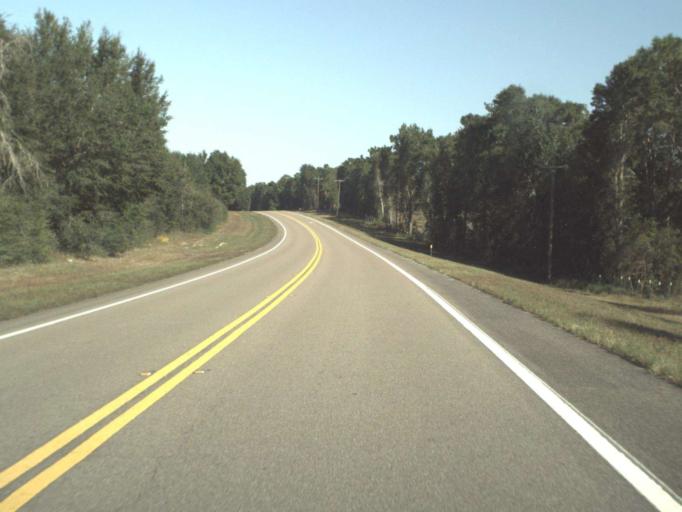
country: US
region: Florida
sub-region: Walton County
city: Freeport
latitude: 30.5486
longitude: -85.9155
